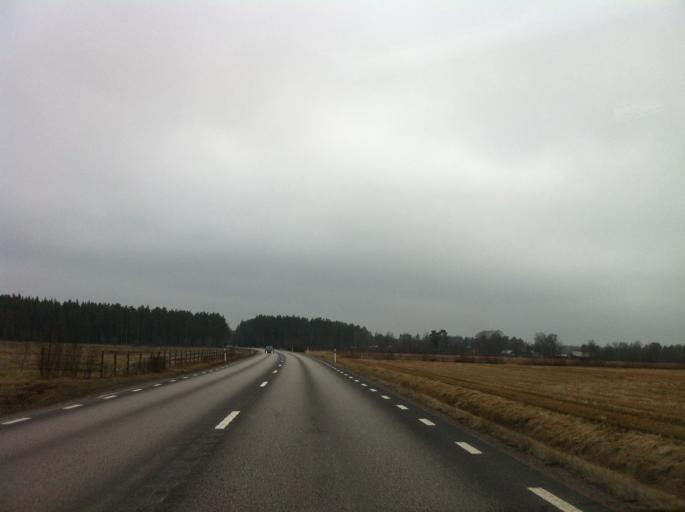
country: SE
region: Vaestra Goetaland
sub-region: Boras Kommun
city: Ganghester
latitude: 57.6684
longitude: 13.0507
